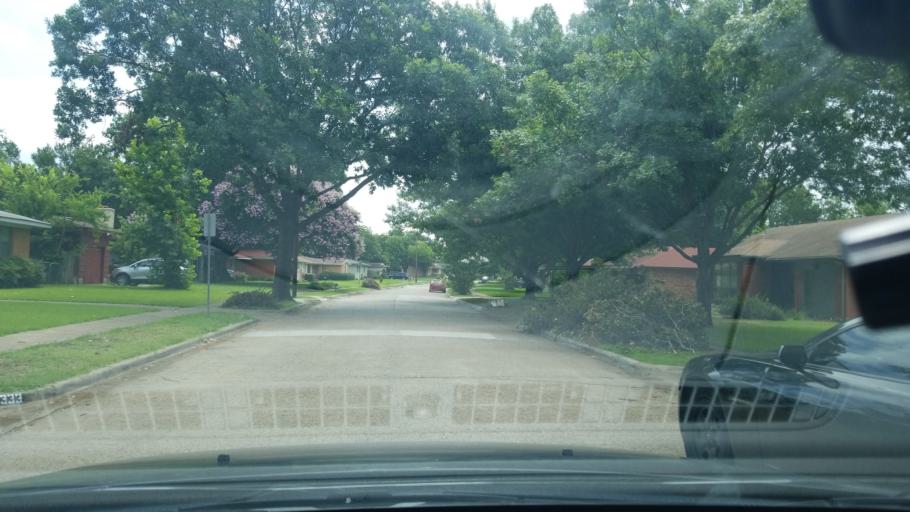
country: US
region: Texas
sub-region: Dallas County
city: Garland
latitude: 32.8291
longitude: -96.6778
